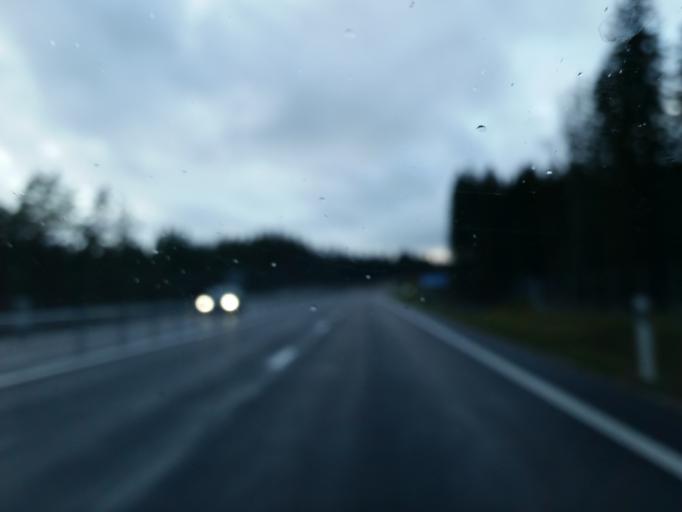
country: SE
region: Vaestra Goetaland
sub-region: Boras Kommun
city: Boras
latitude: 57.6999
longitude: 12.8907
